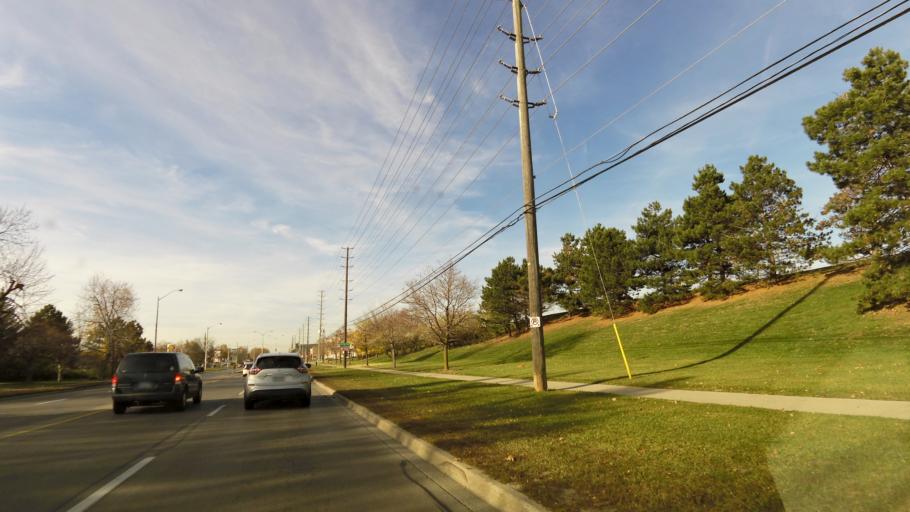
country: CA
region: Ontario
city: Brampton
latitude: 43.7479
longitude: -79.7251
